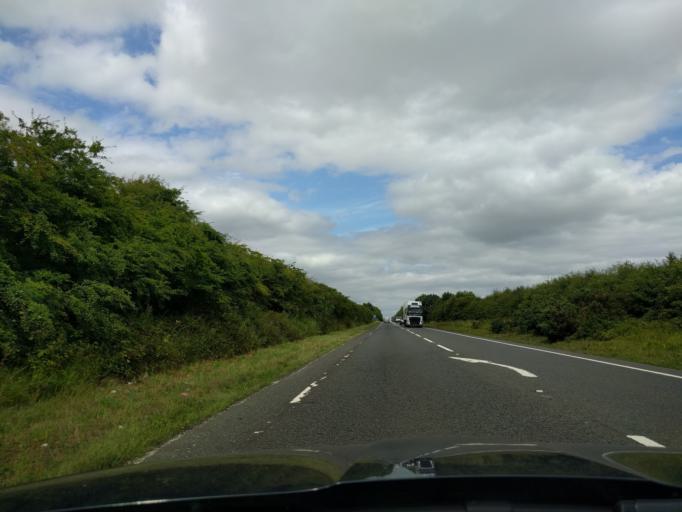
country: GB
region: England
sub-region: Northumberland
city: Alnwick
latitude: 55.4509
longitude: -1.7032
